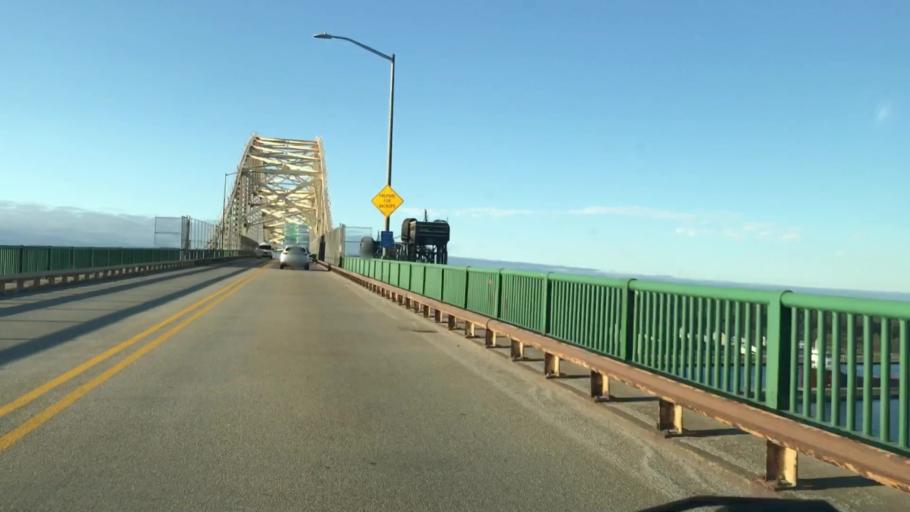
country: US
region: Michigan
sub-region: Chippewa County
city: Sault Ste. Marie
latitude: 46.5051
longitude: -84.3622
